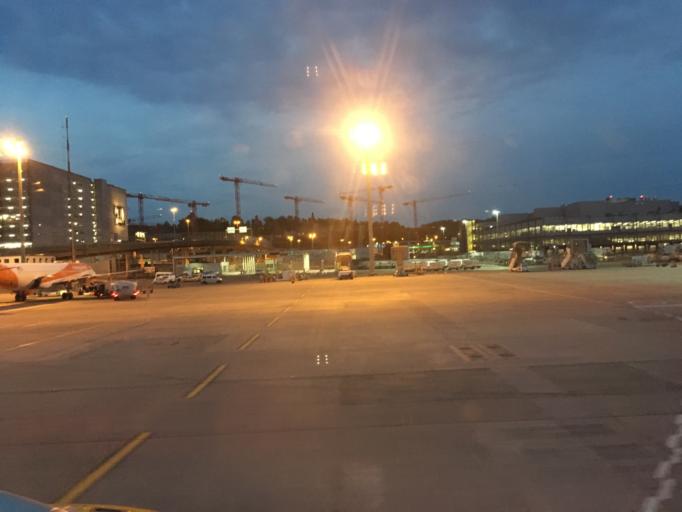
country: CH
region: Zurich
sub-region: Bezirk Buelach
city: Glattbrugg / Rohr/Platten-Balsberg
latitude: 47.4474
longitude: 8.5608
